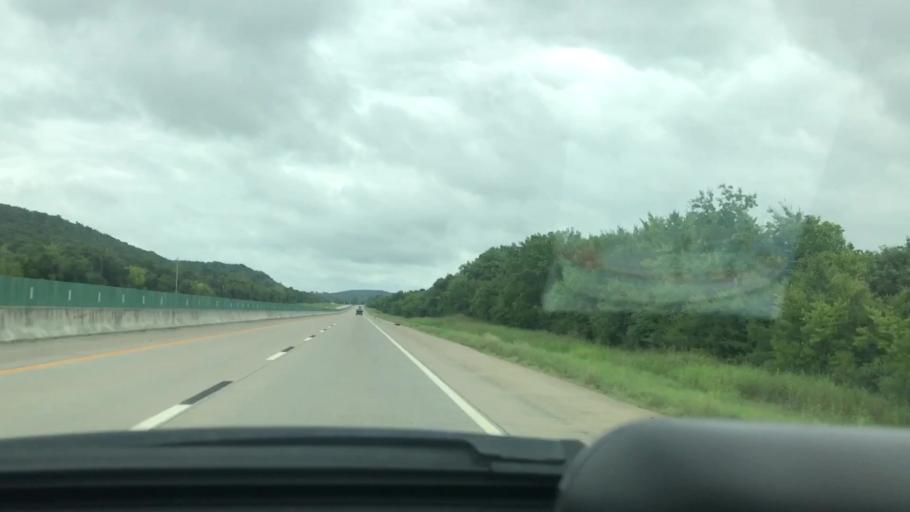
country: US
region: Oklahoma
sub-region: Pittsburg County
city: Krebs
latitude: 35.0813
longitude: -95.7024
